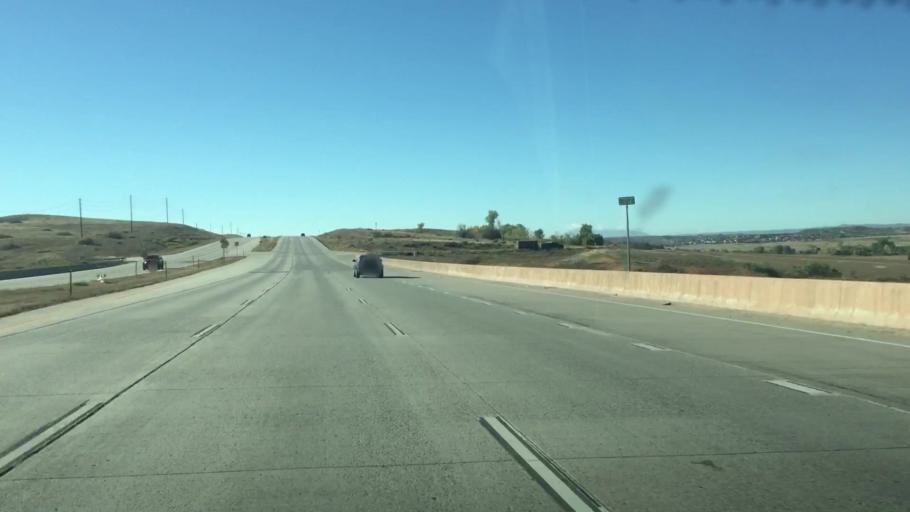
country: US
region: Colorado
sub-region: Douglas County
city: The Pinery
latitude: 39.4756
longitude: -104.7584
